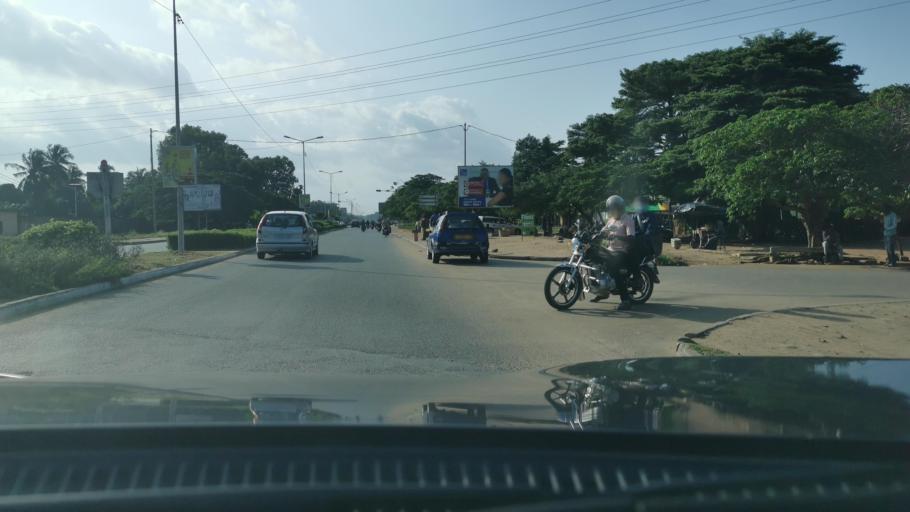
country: TG
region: Maritime
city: Lome
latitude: 6.1577
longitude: 1.2265
